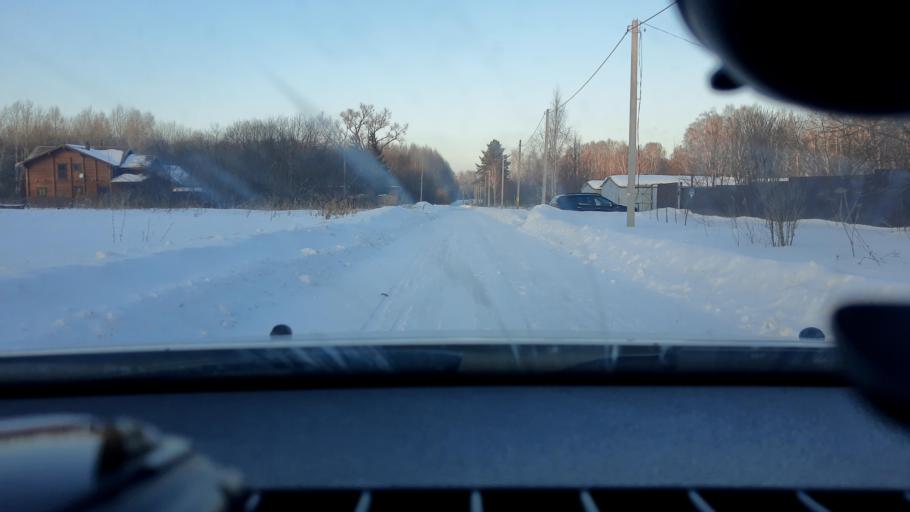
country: RU
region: Bashkortostan
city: Kudeyevskiy
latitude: 54.7977
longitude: 56.6749
